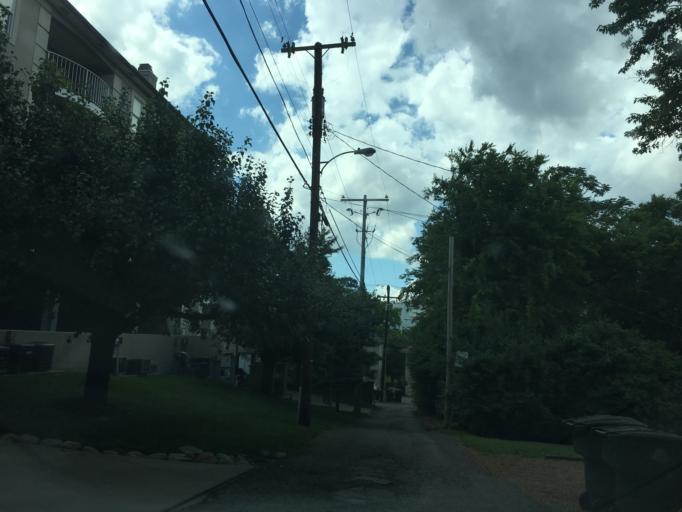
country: US
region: Tennessee
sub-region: Davidson County
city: Nashville
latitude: 36.1406
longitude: -86.8159
